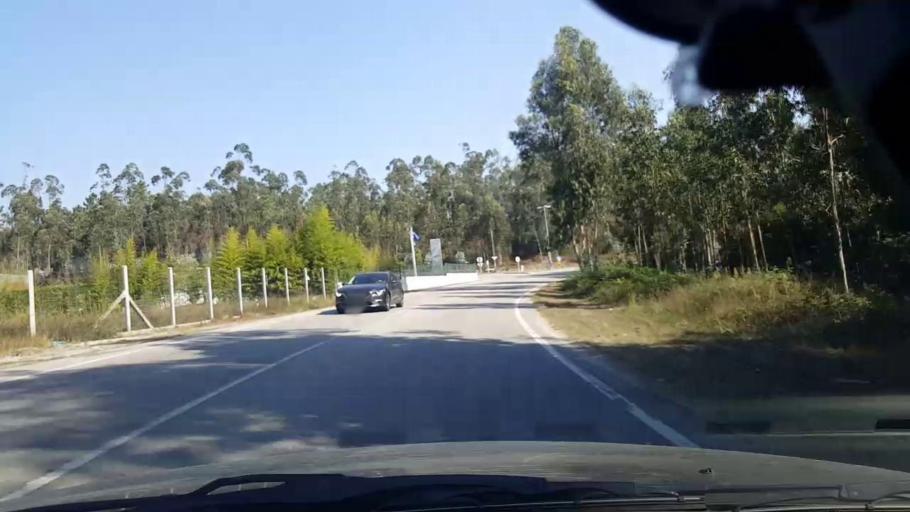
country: PT
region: Porto
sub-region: Vila do Conde
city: Arvore
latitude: 41.3553
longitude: -8.6880
